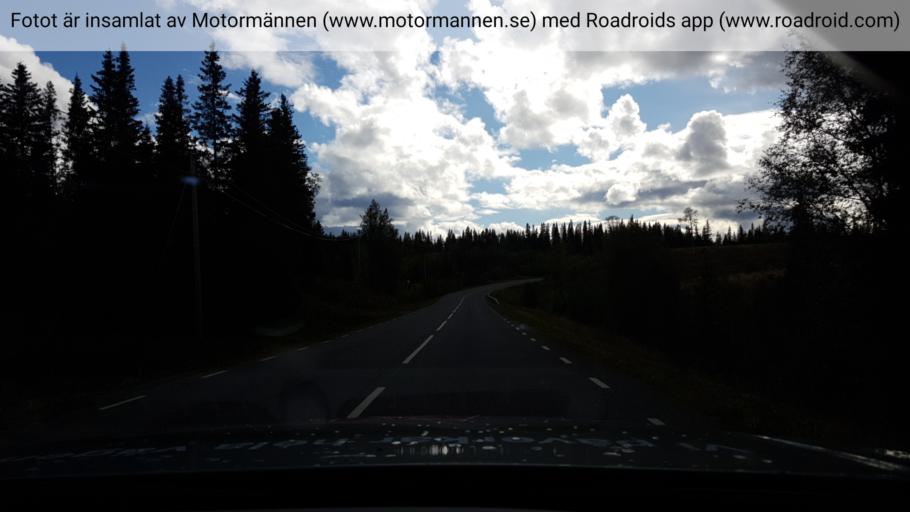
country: SE
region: Jaemtland
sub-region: Are Kommun
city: Are
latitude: 63.5774
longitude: 13.0207
